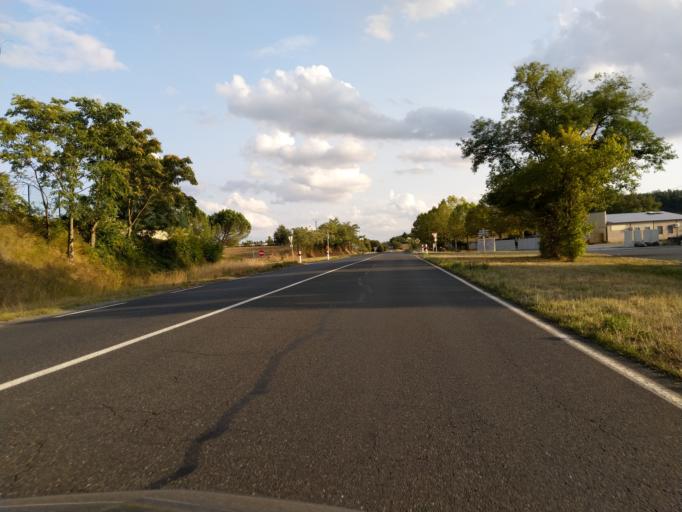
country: FR
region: Midi-Pyrenees
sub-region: Departement du Tarn
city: Realmont
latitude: 43.8068
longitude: 2.1828
